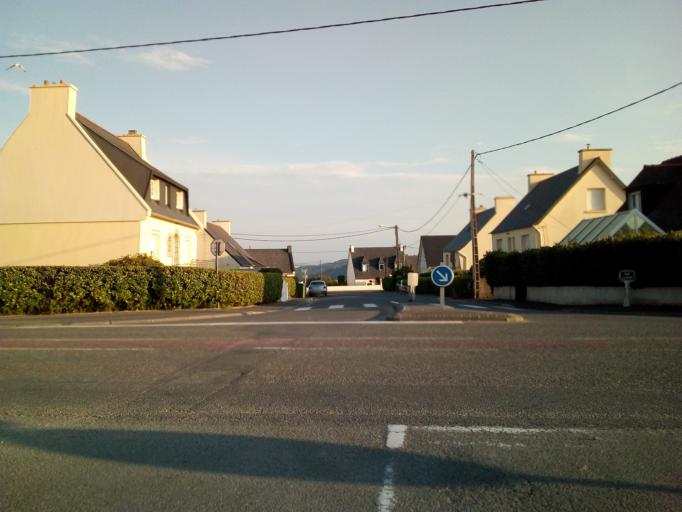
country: FR
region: Brittany
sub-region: Departement du Finistere
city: Landivisiau
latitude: 48.5017
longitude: -4.0741
